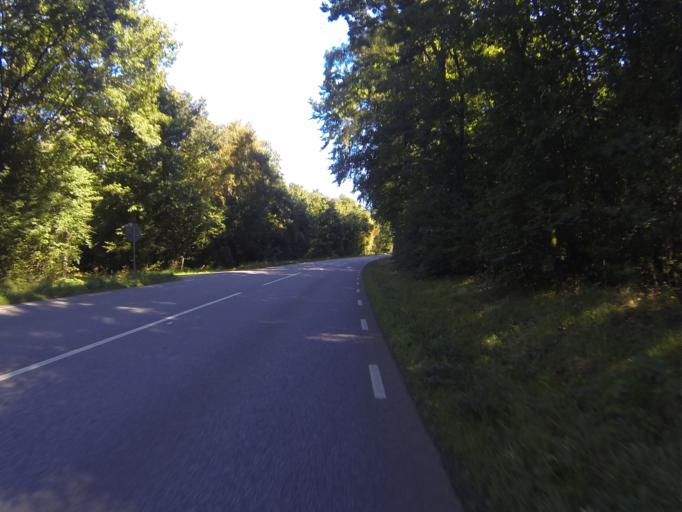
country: SE
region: Skane
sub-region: Hoors Kommun
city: Loberod
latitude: 55.7339
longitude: 13.3926
